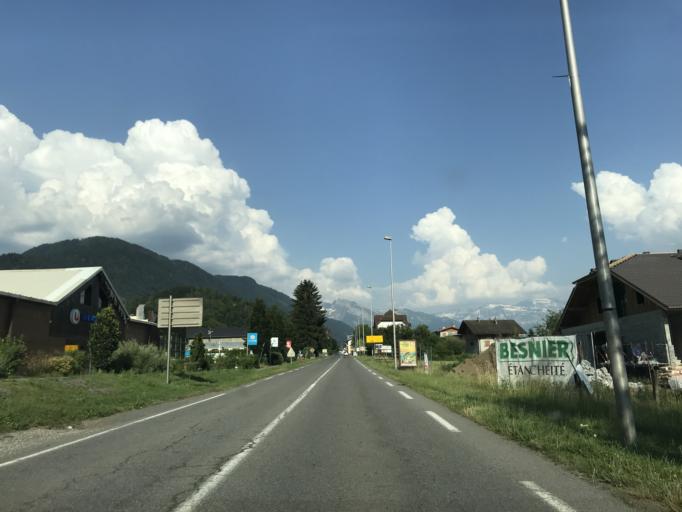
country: FR
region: Rhone-Alpes
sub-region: Departement de la Haute-Savoie
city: Taninges
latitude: 46.1084
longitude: 6.5832
